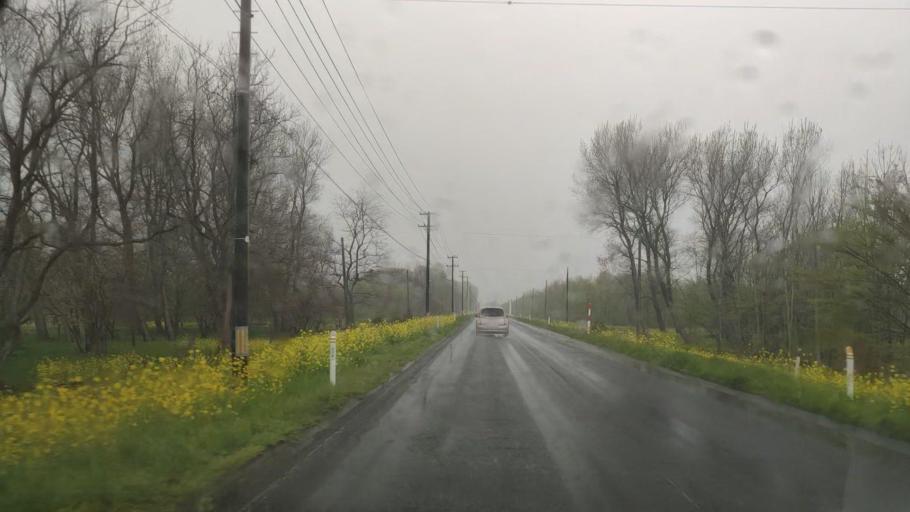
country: JP
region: Akita
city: Tenno
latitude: 39.9539
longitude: 139.9459
